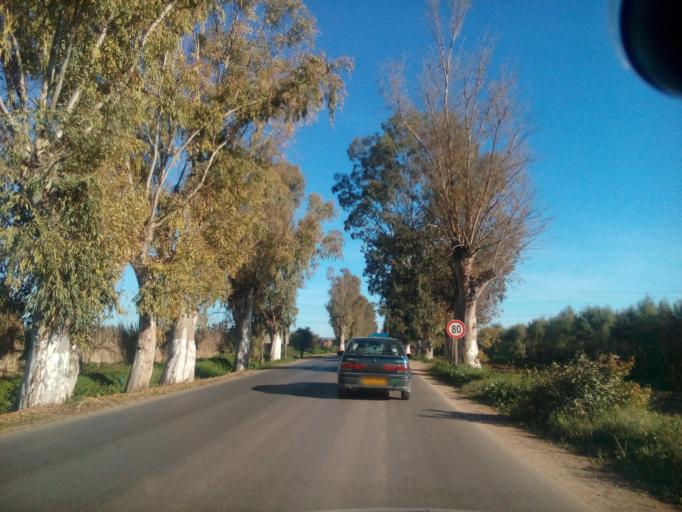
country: DZ
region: Mostaganem
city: Mostaganem
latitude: 35.9053
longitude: 0.1920
